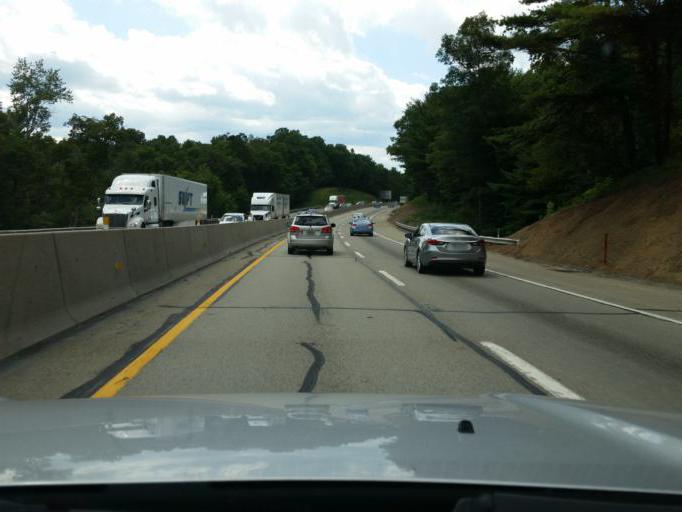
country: US
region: Pennsylvania
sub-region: Fulton County
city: McConnellsburg
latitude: 40.0371
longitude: -77.9971
